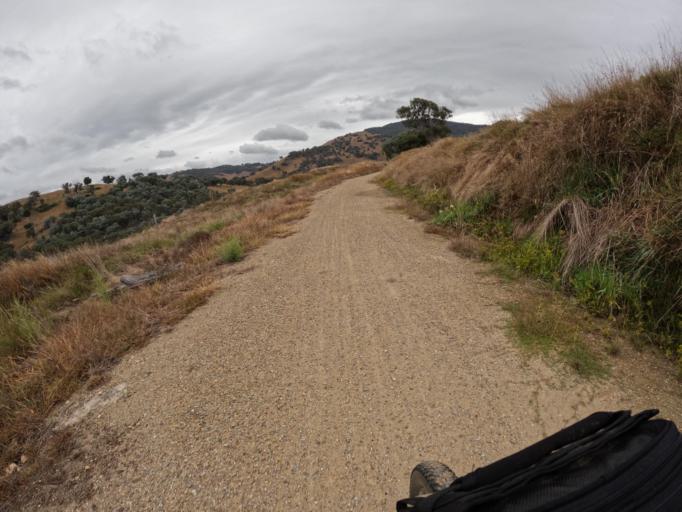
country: AU
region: New South Wales
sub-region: Albury Municipality
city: East Albury
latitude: -36.1809
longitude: 147.3753
